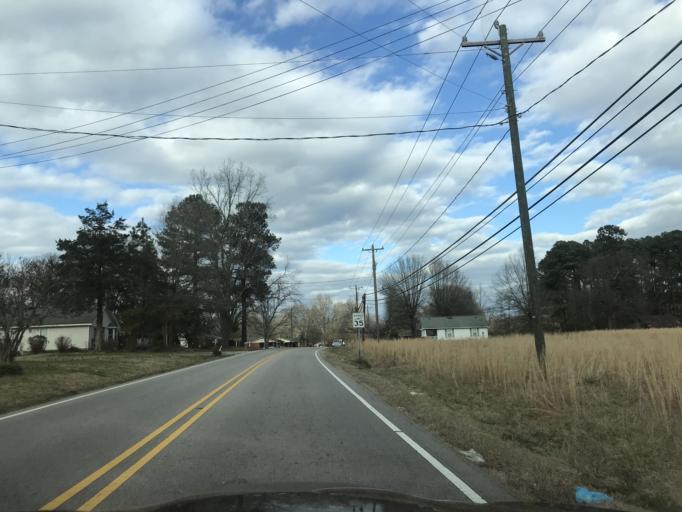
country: US
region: North Carolina
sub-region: Durham County
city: Gorman
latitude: 35.9715
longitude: -78.8297
